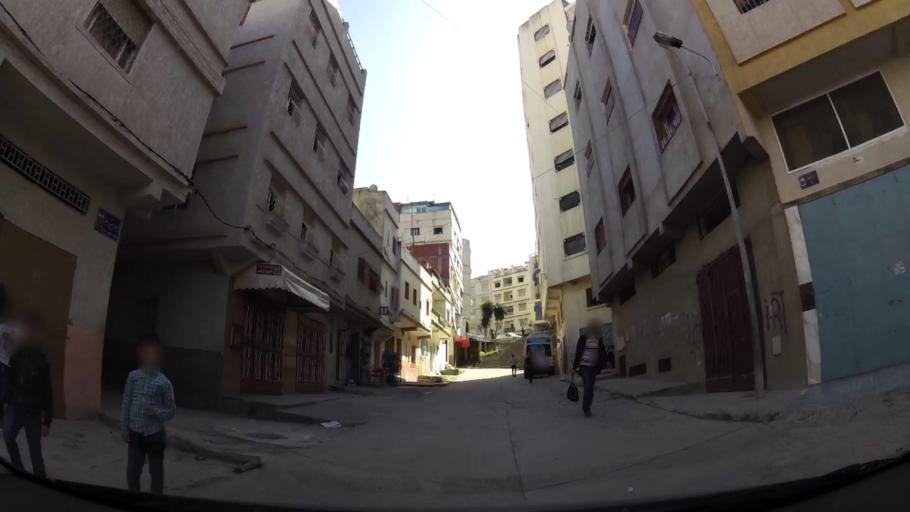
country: MA
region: Tanger-Tetouan
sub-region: Tanger-Assilah
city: Tangier
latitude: 35.7476
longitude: -5.8080
